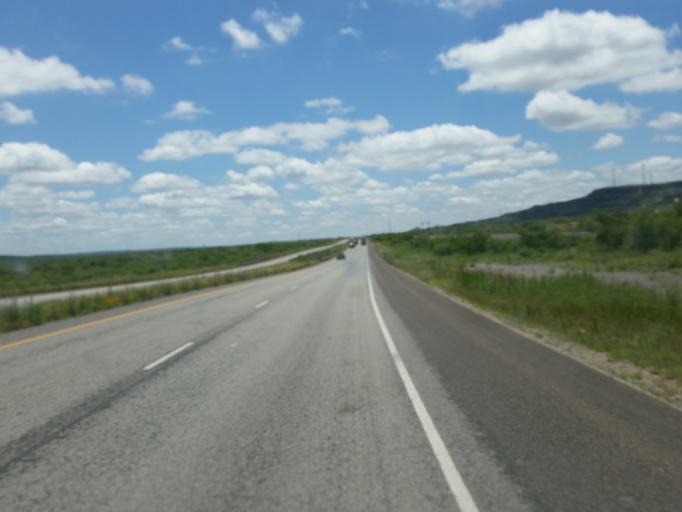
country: US
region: Texas
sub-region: Scurry County
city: Snyder
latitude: 32.9769
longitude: -101.1032
